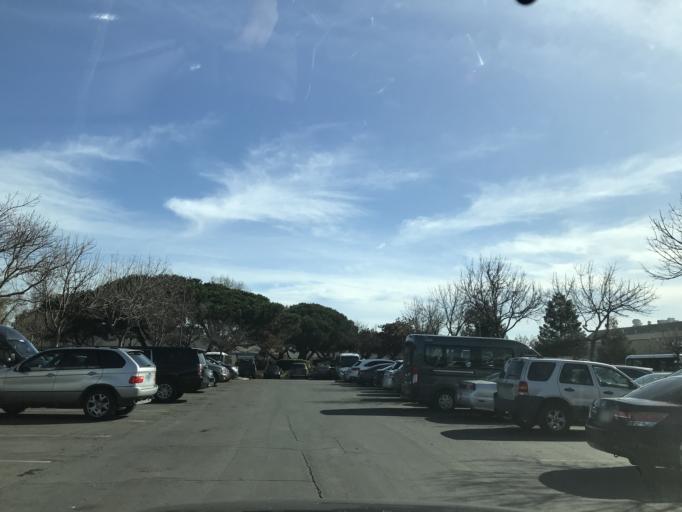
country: US
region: California
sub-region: San Mateo County
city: East Palo Alto
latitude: 37.4783
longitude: -122.1502
